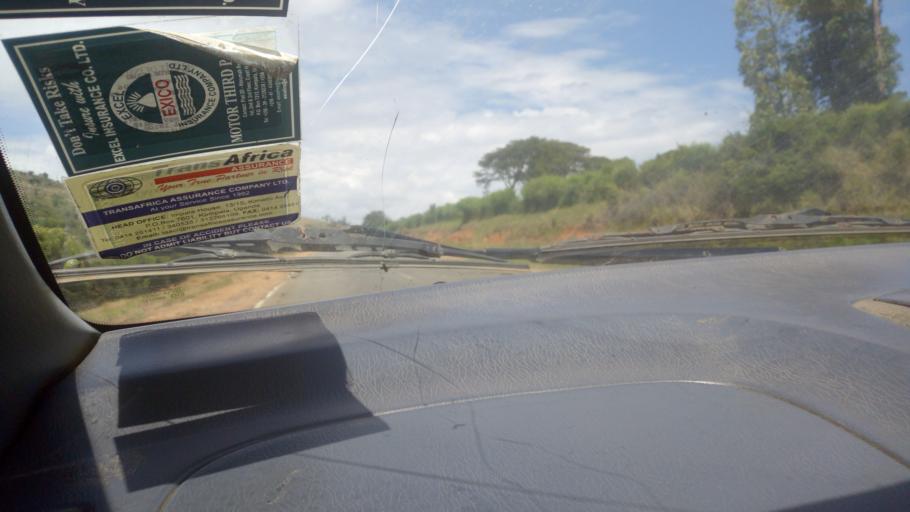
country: UG
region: Western Region
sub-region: Buhweju District
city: Buhweju
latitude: -0.2456
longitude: 30.5495
